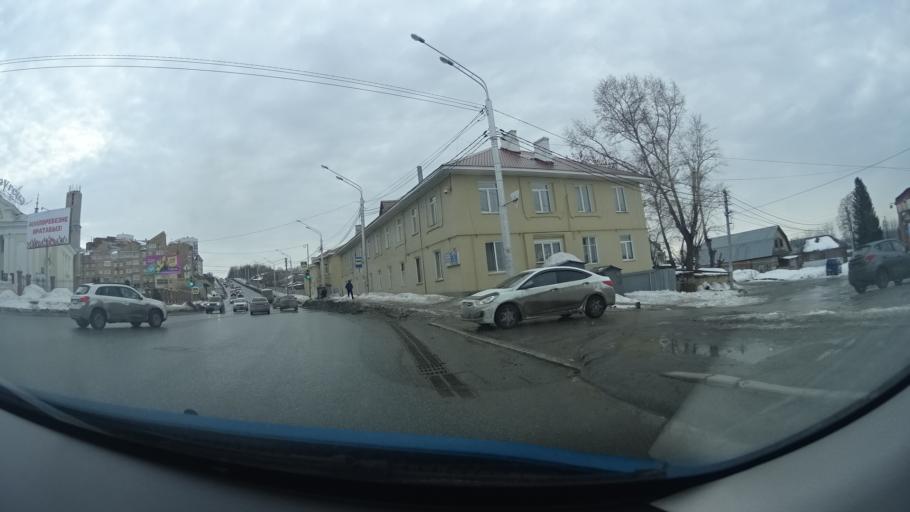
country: RU
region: Bashkortostan
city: Ufa
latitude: 54.7059
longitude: 55.9732
